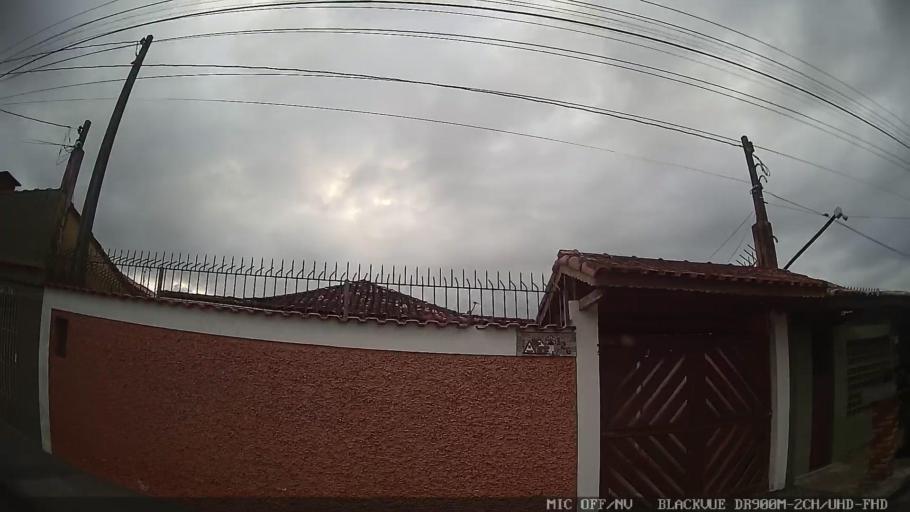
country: BR
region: Sao Paulo
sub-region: Itanhaem
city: Itanhaem
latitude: -24.1942
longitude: -46.8147
